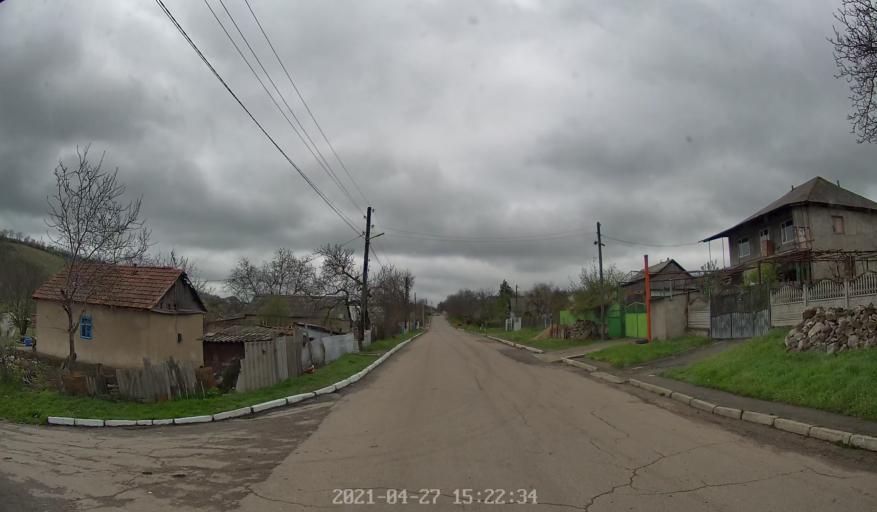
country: MD
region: Chisinau
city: Vadul lui Voda
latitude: 47.0274
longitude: 29.0247
